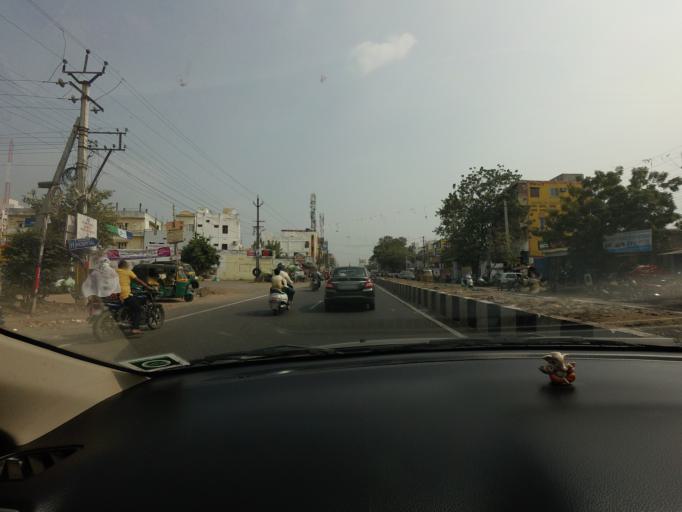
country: IN
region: Andhra Pradesh
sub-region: Krishna
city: Yanamalakuduru
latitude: 16.4843
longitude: 80.6849
